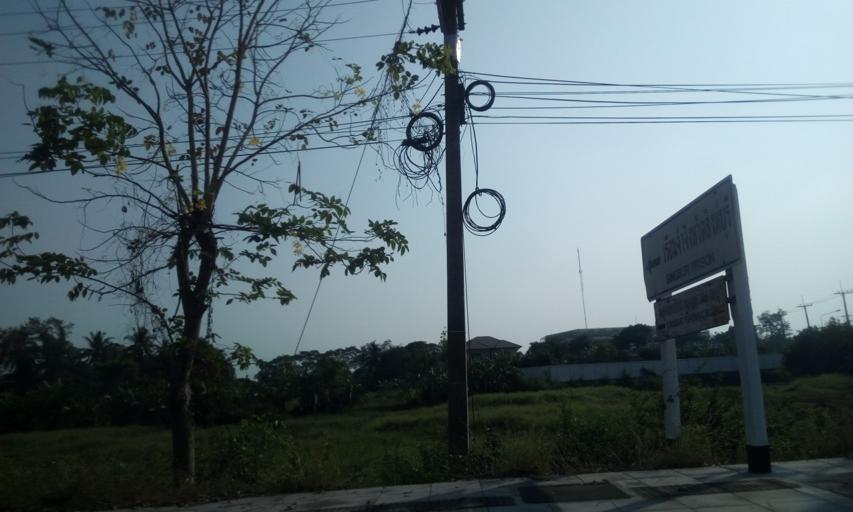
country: TH
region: Sing Buri
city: Sing Buri
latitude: 14.8707
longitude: 100.4021
